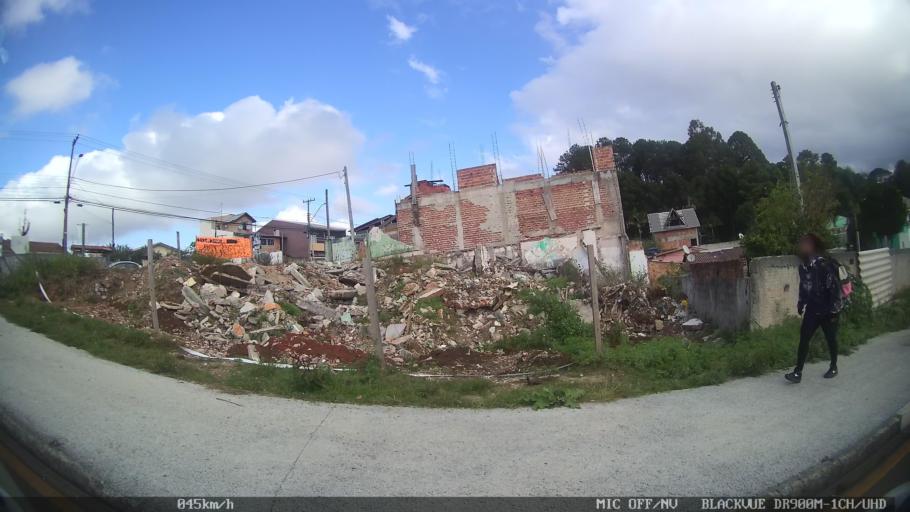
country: BR
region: Parana
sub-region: Pinhais
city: Pinhais
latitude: -25.3960
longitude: -49.1822
